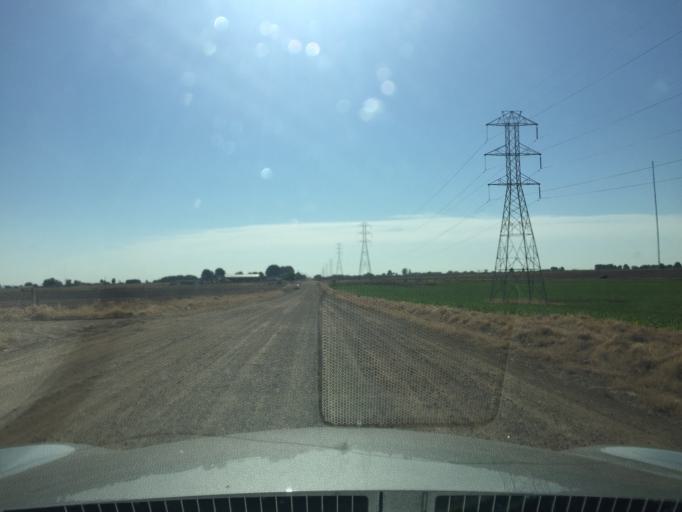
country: US
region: Colorado
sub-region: Boulder County
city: Erie
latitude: 40.0582
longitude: -105.0222
